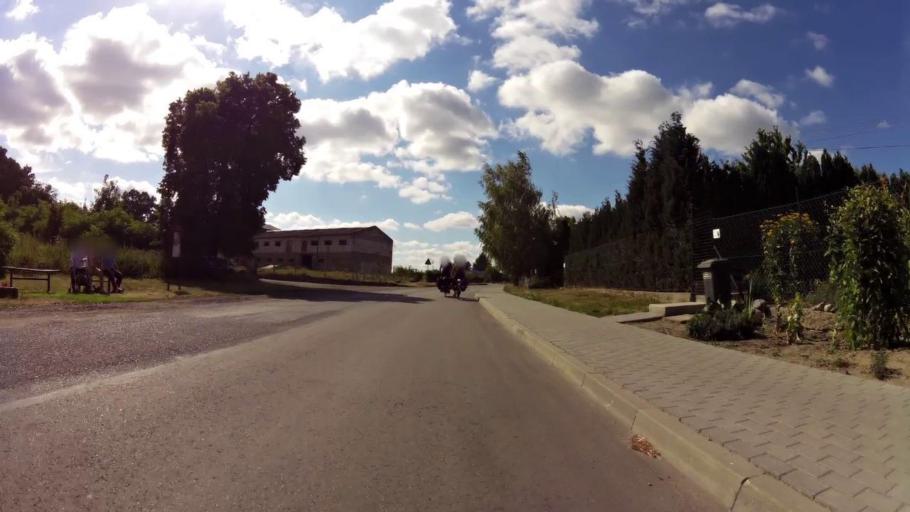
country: PL
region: West Pomeranian Voivodeship
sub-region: Powiat lobeski
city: Lobez
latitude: 53.6433
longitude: 15.6716
